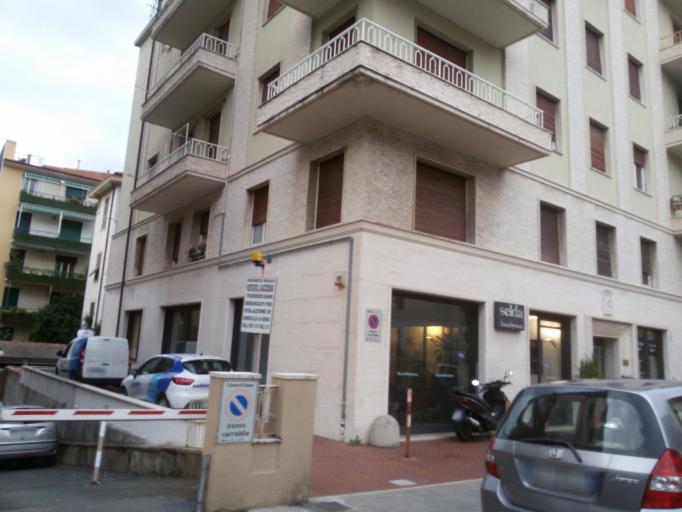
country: IT
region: Liguria
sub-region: Provincia di Genova
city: Chiavari
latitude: 44.3194
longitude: 9.3194
